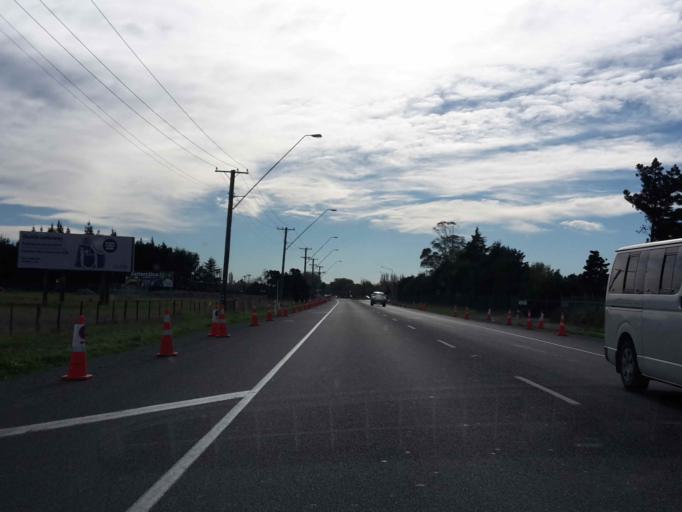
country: NZ
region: Canterbury
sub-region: Christchurch City
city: Christchurch
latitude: -43.4896
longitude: 172.5518
